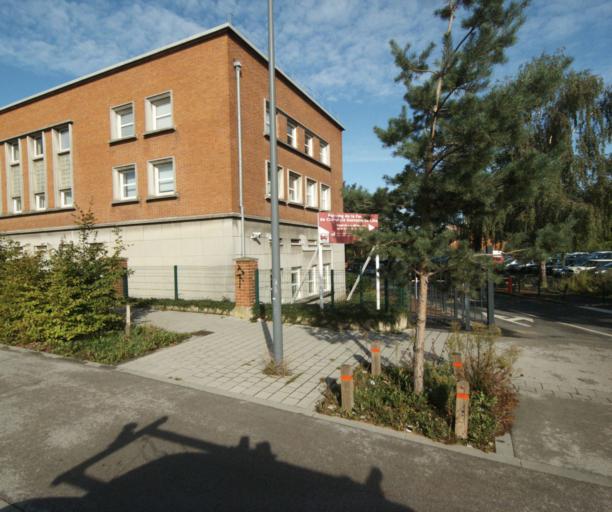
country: FR
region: Nord-Pas-de-Calais
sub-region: Departement du Nord
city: Loos
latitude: 50.6141
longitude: 3.0381
